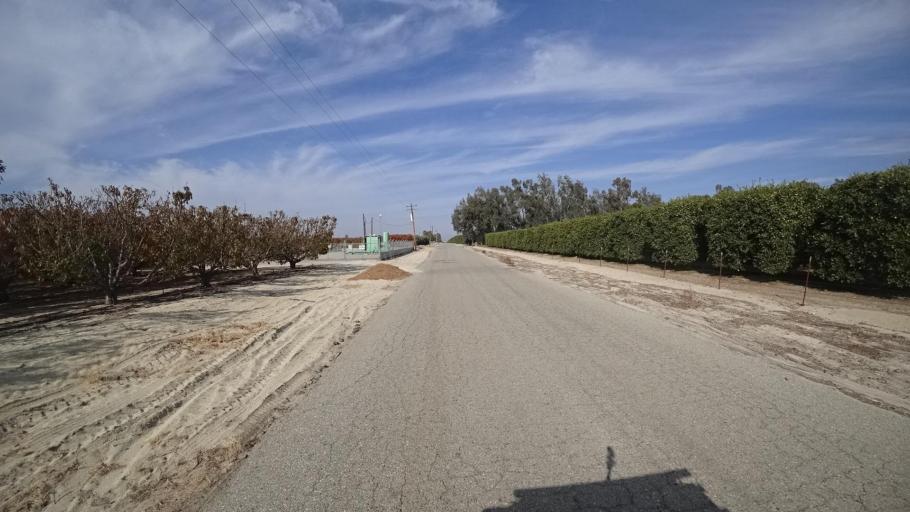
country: US
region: California
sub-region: Kern County
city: Arvin
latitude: 35.2738
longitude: -118.7527
